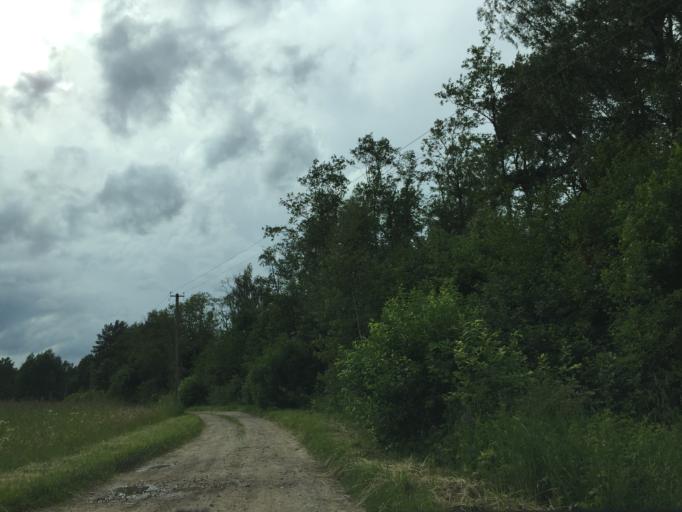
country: LV
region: Apes Novads
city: Ape
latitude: 57.4201
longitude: 26.3759
